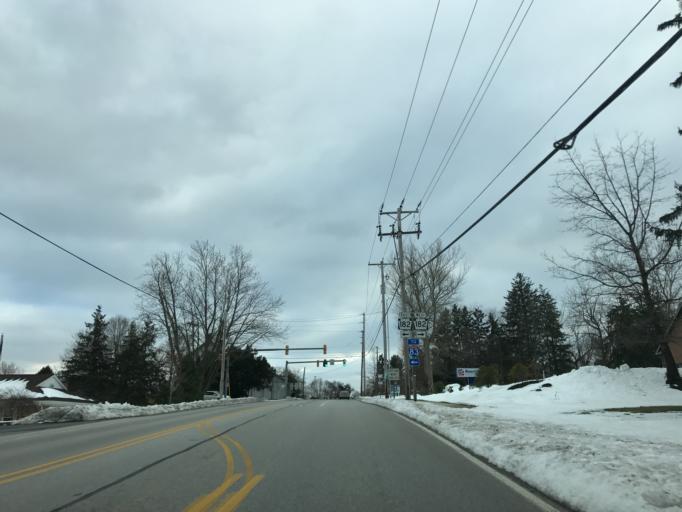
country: US
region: Pennsylvania
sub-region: York County
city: Jacobus
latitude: 39.9115
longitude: -76.7136
